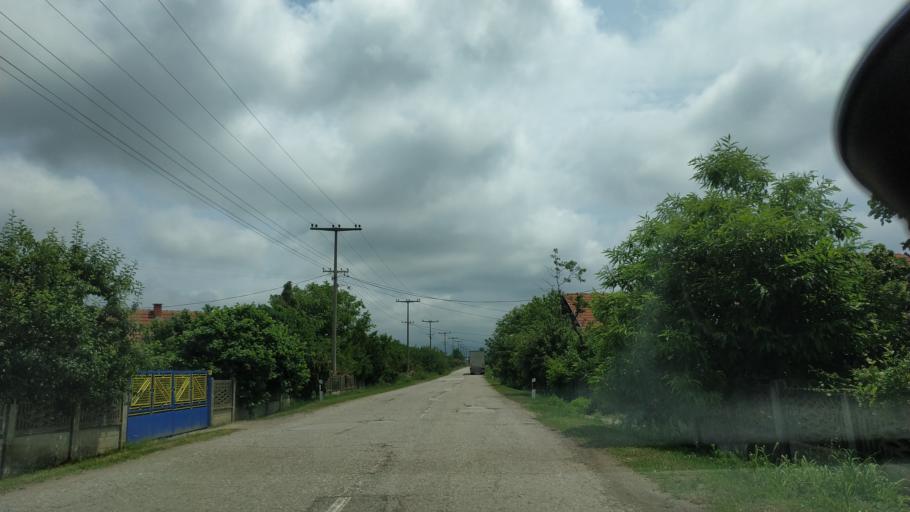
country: RS
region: Central Serbia
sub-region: Nisavski Okrug
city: Aleksinac
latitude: 43.4399
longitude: 21.7150
